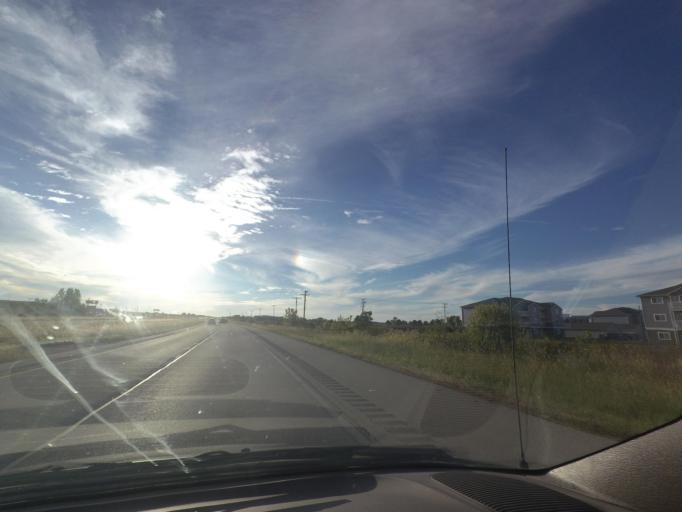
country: US
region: Illinois
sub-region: Sangamon County
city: Jerome
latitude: 39.7522
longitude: -89.7378
